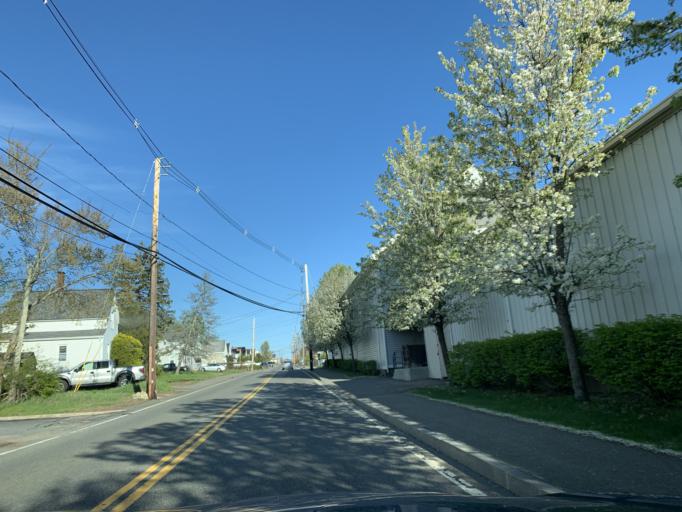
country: US
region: Massachusetts
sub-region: Norfolk County
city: Stoughton
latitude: 42.1268
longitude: -71.1122
